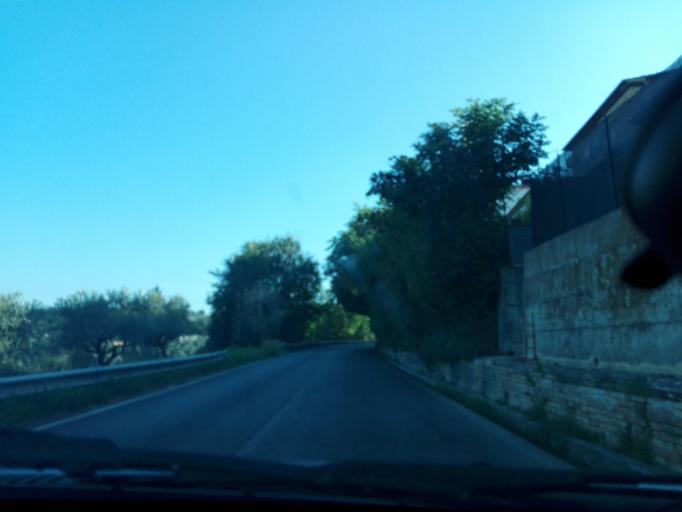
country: IT
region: Abruzzo
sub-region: Provincia di Pescara
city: Cappelle sul Tavo
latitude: 42.4685
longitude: 14.1051
